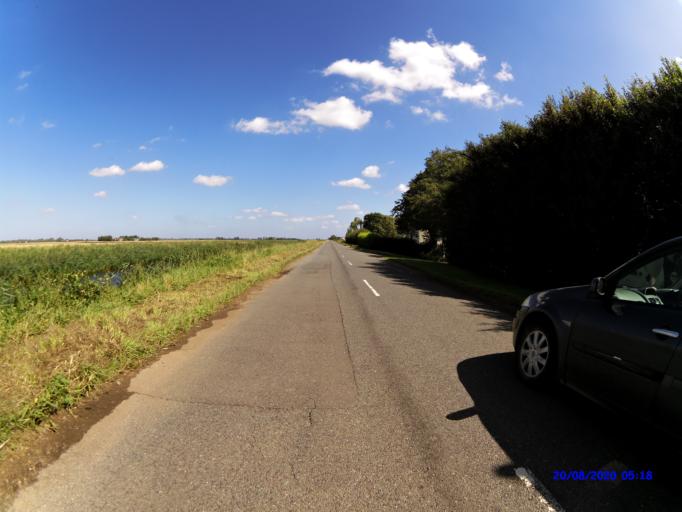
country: GB
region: England
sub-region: Cambridgeshire
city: Whittlesey
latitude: 52.5252
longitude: -0.1105
